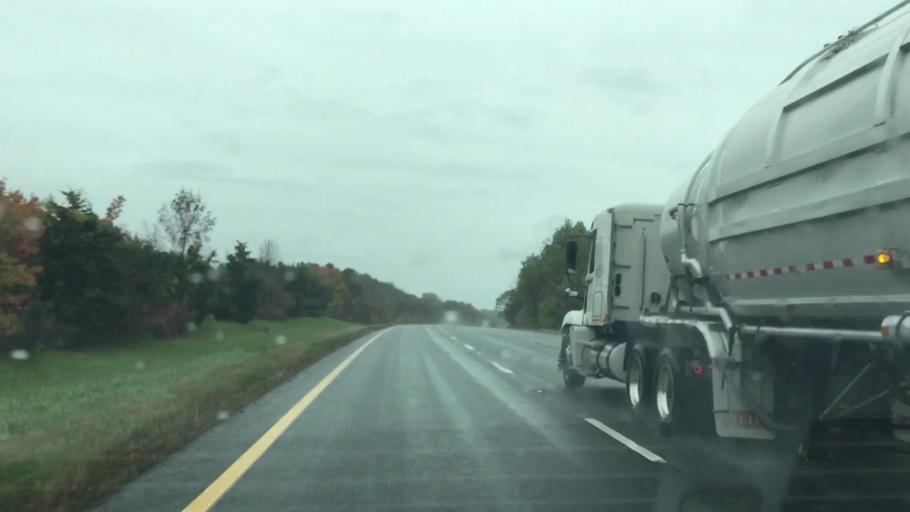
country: US
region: Massachusetts
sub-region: Essex County
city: Merrimac
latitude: 42.8184
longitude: -71.0201
